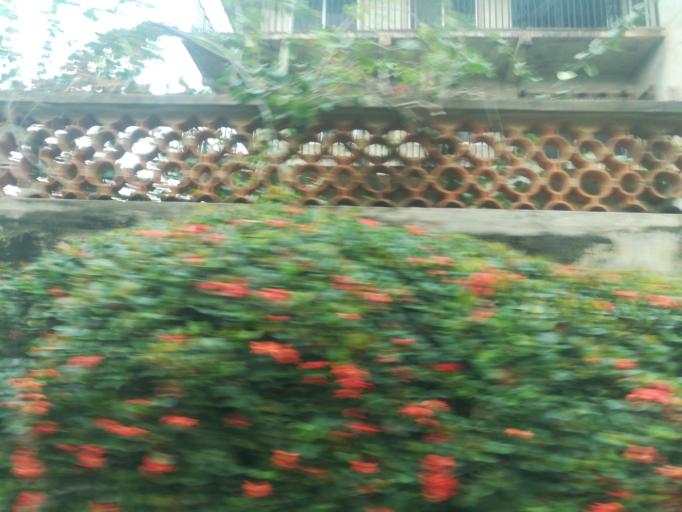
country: NG
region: Oyo
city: Ibadan
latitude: 7.3761
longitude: 3.8572
